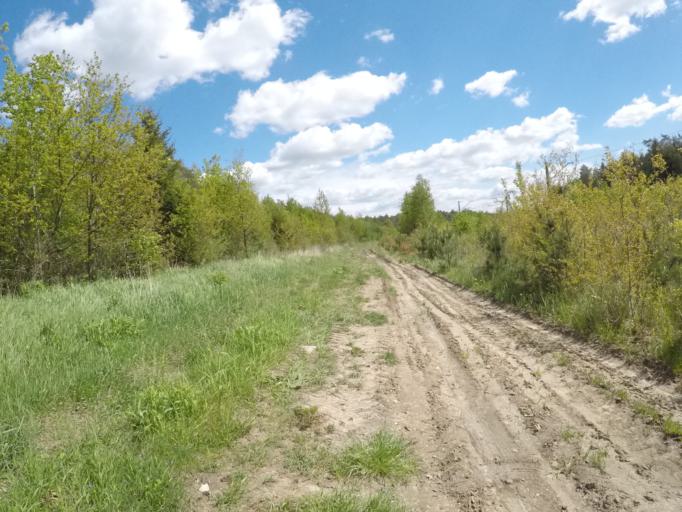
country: PL
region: Swietokrzyskie
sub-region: Powiat kielecki
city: Kostomloty Pierwsze
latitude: 50.9199
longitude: 20.6198
